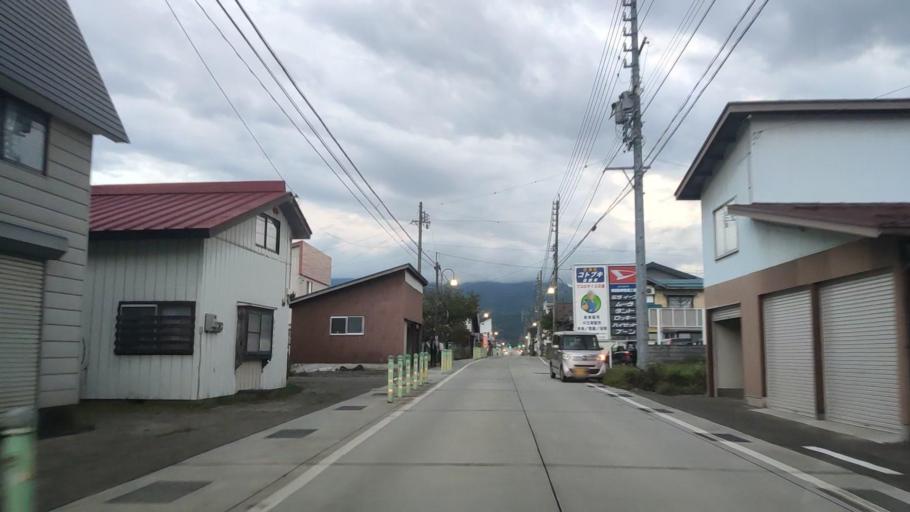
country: JP
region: Nagano
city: Iiyama
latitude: 36.8651
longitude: 138.4067
